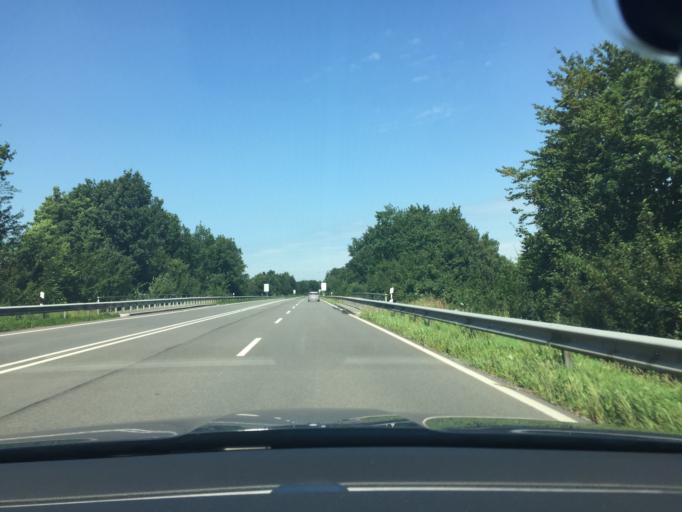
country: DE
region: Lower Saxony
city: Ostrhauderfehn
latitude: 53.1237
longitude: 7.6600
